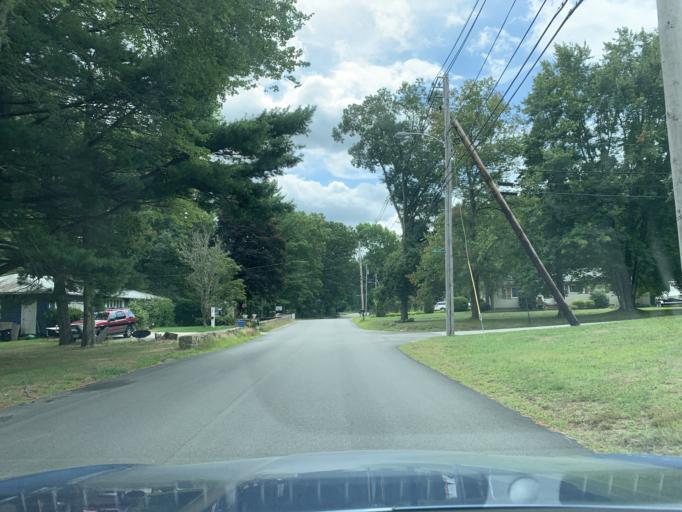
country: US
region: Rhode Island
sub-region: Kent County
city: West Warwick
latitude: 41.7385
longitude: -71.5769
